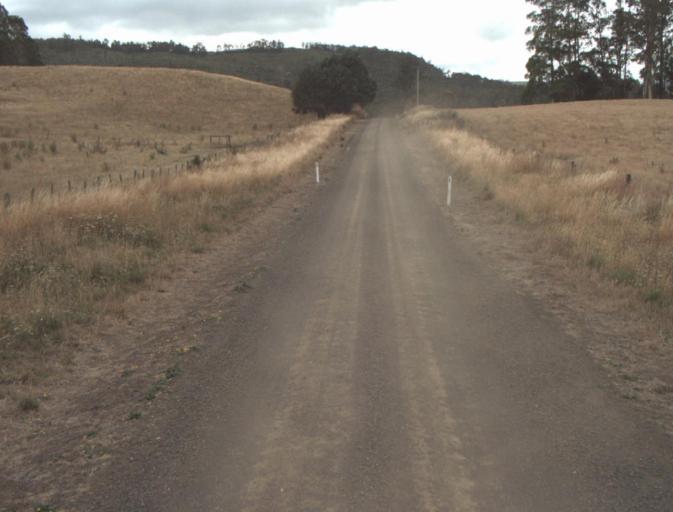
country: AU
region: Tasmania
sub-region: Northern Midlands
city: Evandale
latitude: -41.4611
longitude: 147.4554
